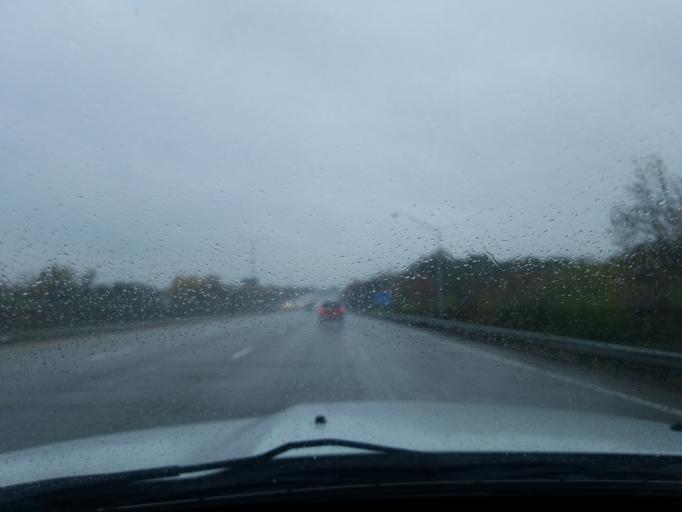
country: US
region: Kentucky
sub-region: Jefferson County
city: Shively
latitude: 38.2197
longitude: -85.8225
